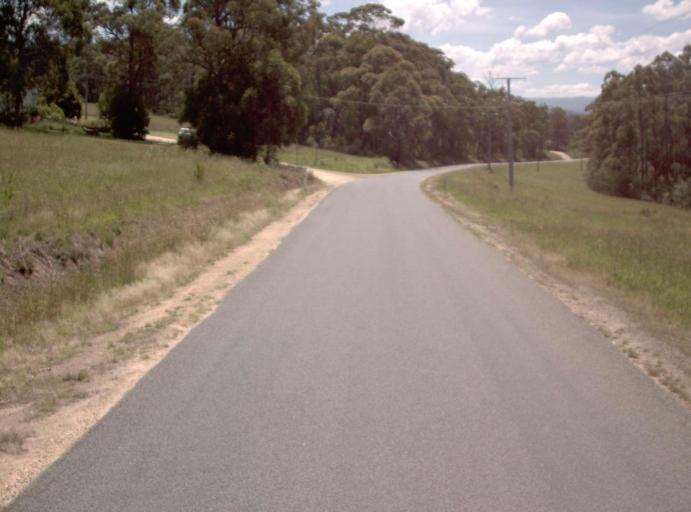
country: AU
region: New South Wales
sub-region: Bombala
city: Bombala
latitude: -37.5534
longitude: 148.9378
